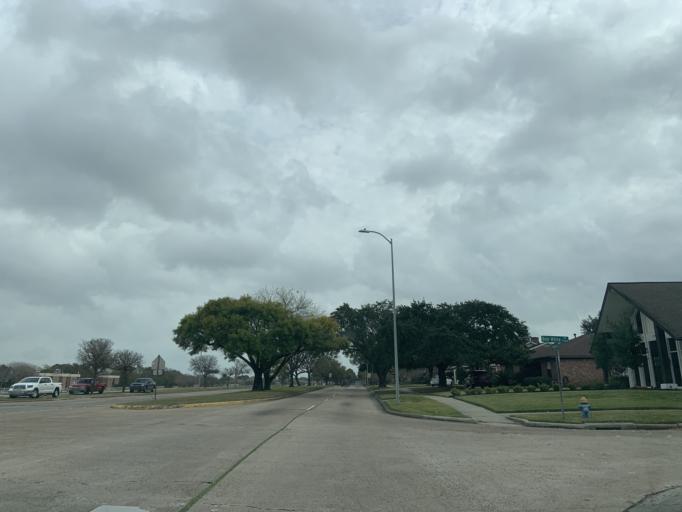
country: US
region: Texas
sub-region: Harris County
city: Bellaire
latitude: 29.6768
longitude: -95.5028
